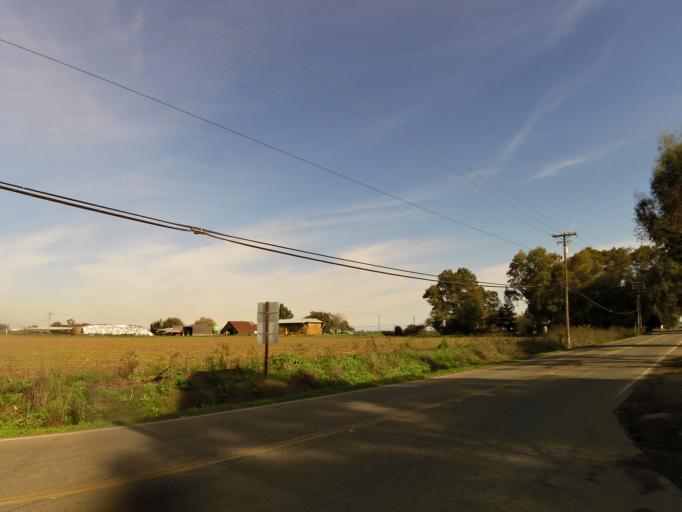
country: US
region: California
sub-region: San Joaquin County
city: Thornton
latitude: 38.3212
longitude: -121.4203
